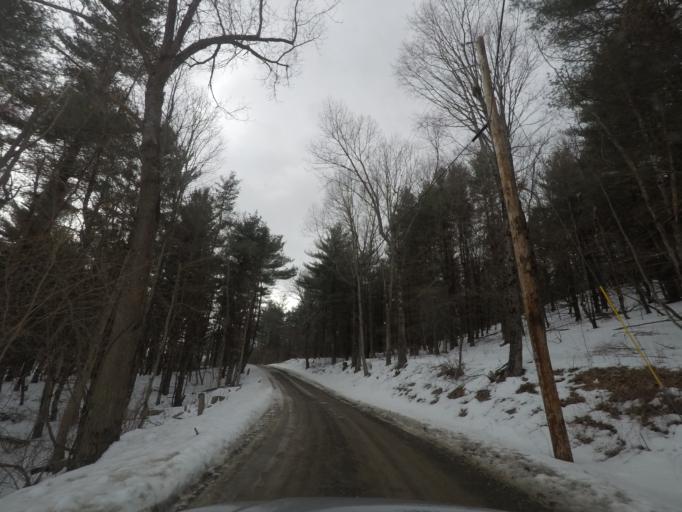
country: US
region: New York
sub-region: Saratoga County
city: Waterford
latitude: 42.7870
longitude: -73.6087
